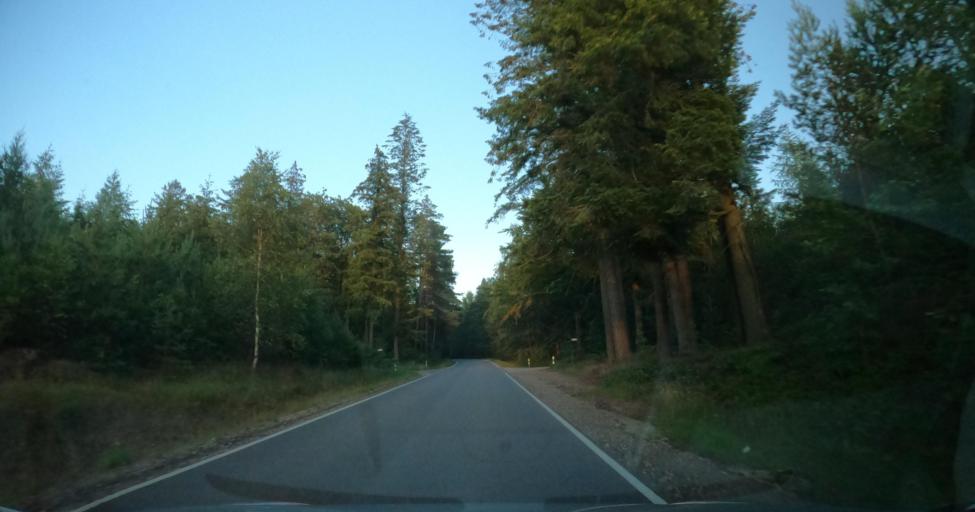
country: PL
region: Pomeranian Voivodeship
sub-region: Powiat leborski
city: Lebork
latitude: 54.4998
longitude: 17.8339
